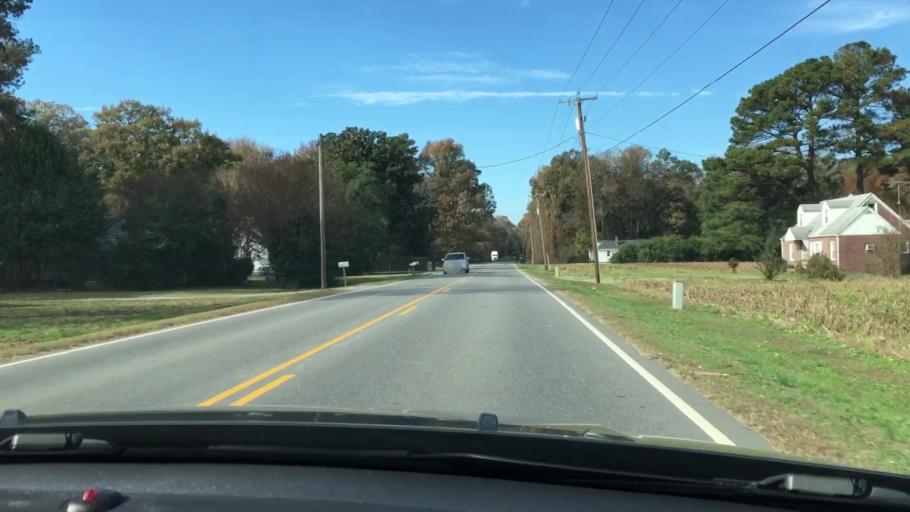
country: US
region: Virginia
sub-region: King William County
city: West Point
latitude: 37.5734
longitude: -76.8393
